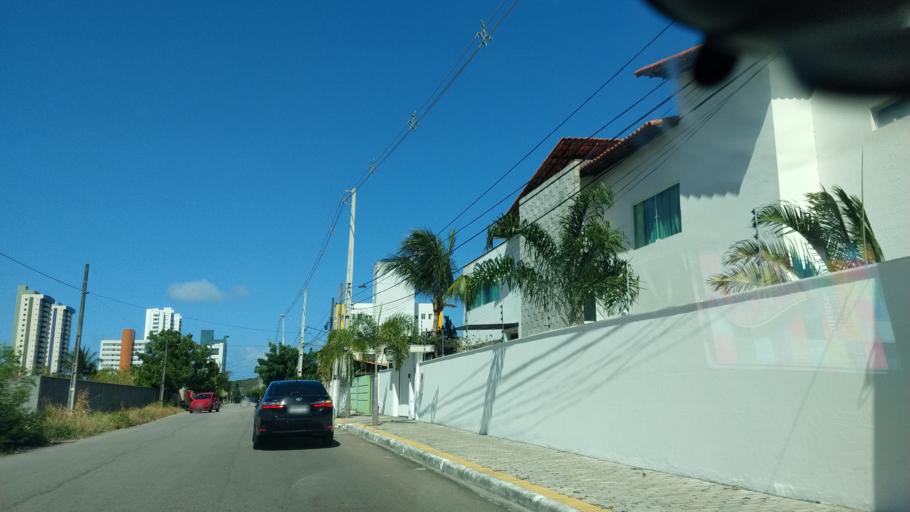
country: BR
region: Rio Grande do Norte
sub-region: Natal
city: Natal
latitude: -5.8699
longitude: -35.1934
